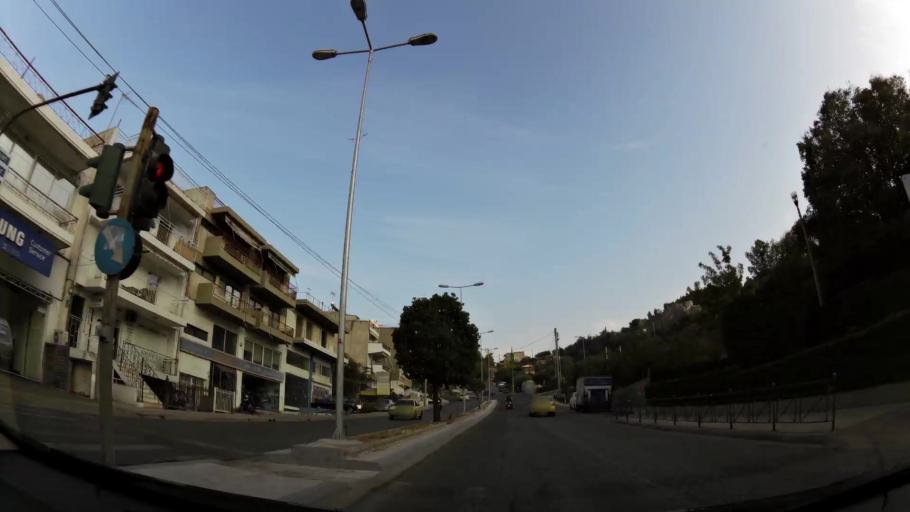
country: GR
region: Attica
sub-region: Nomarchia Athinas
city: Galatsi
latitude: 38.0089
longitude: 23.7595
